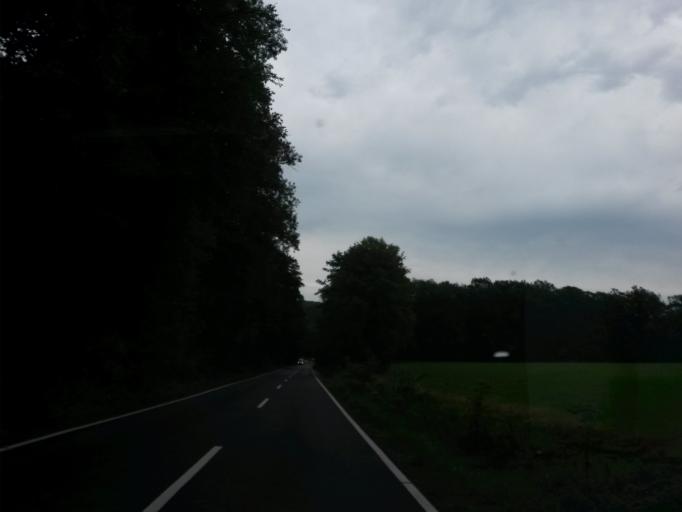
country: DE
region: North Rhine-Westphalia
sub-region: Regierungsbezirk Koln
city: Numbrecht
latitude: 50.9169
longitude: 7.5441
